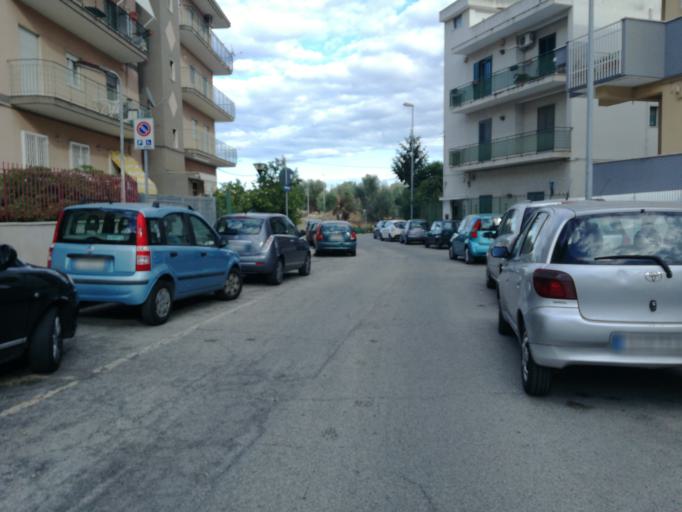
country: IT
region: Apulia
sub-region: Provincia di Bari
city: Triggiano
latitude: 41.0673
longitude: 16.9372
